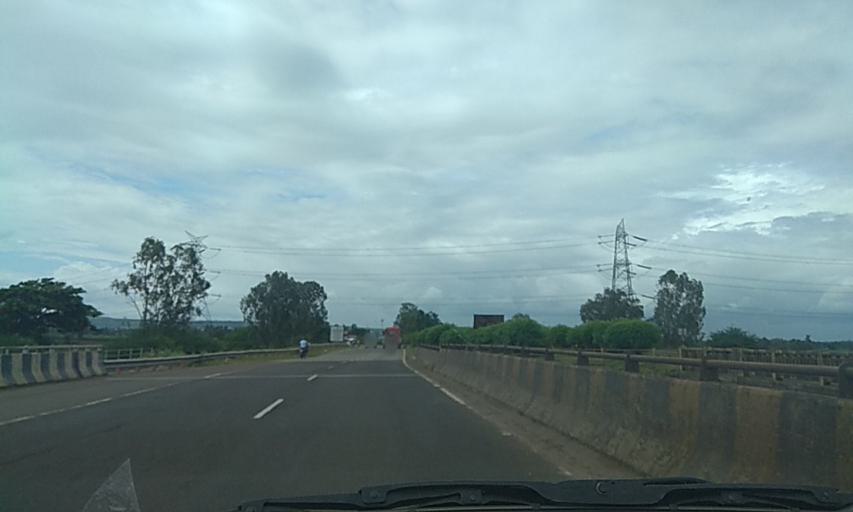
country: IN
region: Maharashtra
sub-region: Kolhapur
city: Kagal
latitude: 16.5542
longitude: 74.3178
